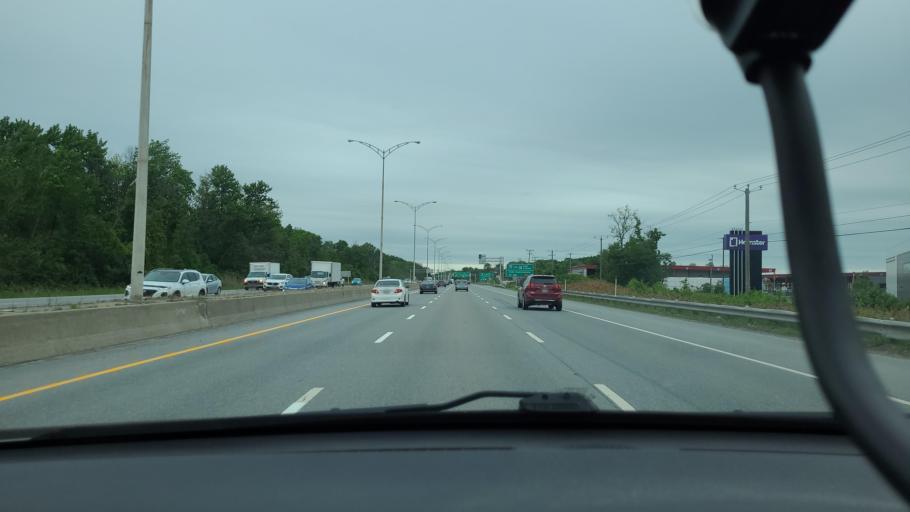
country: CA
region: Quebec
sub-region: Lanaudiere
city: Terrebonne
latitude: 45.6364
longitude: -73.6530
